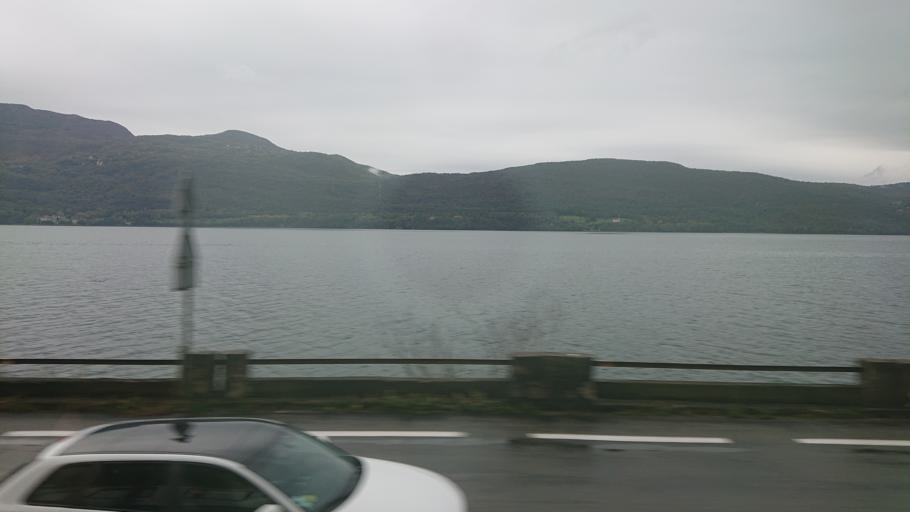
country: FR
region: Rhone-Alpes
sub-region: Departement de la Savoie
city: Chatillon
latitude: 45.7767
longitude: 5.8656
